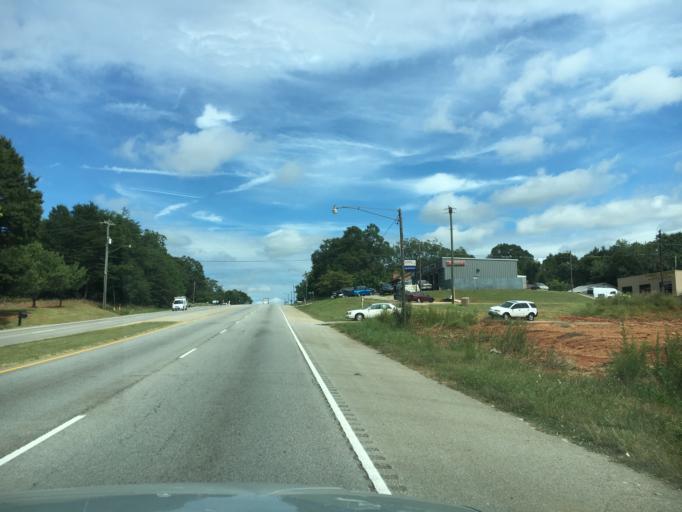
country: US
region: South Carolina
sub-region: Spartanburg County
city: Lyman
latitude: 34.9556
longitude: -82.1376
